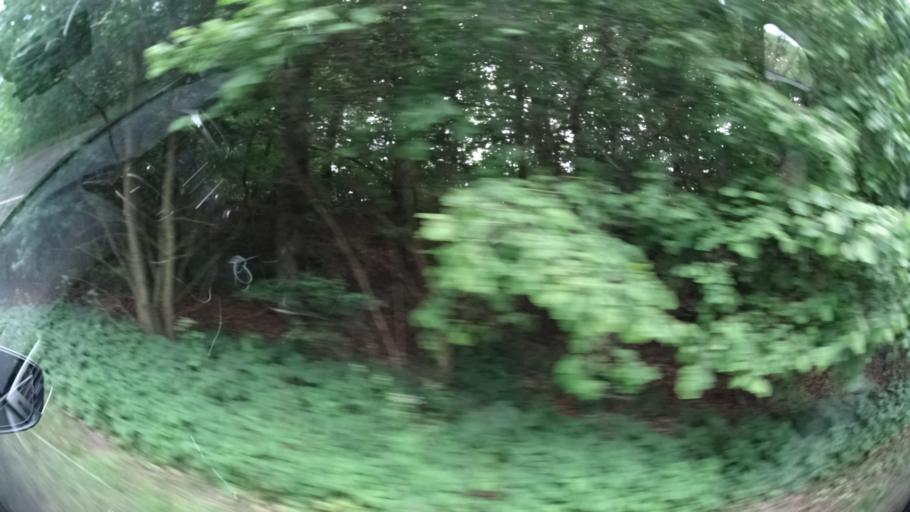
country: DK
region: Central Jutland
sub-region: Syddjurs Kommune
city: Ryomgard
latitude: 56.4063
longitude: 10.5607
